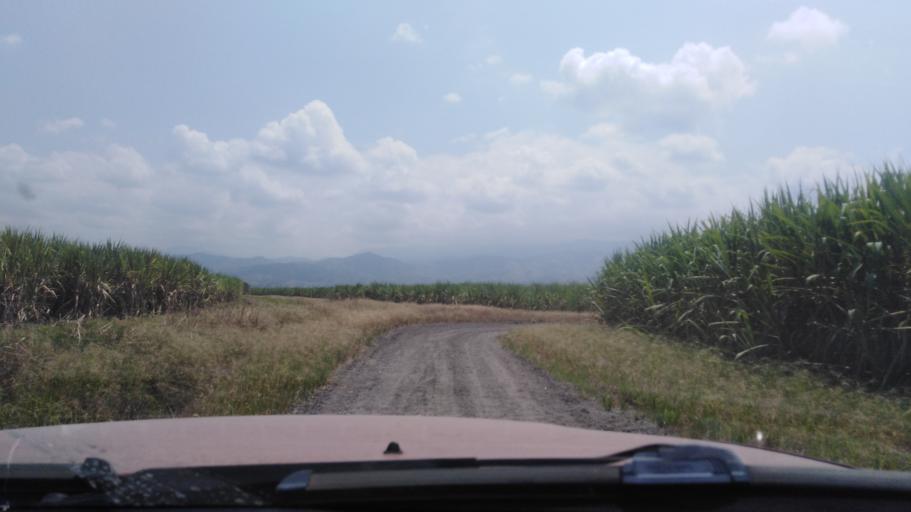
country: CO
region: Valle del Cauca
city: San Pedro
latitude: 3.9974
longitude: -76.2725
